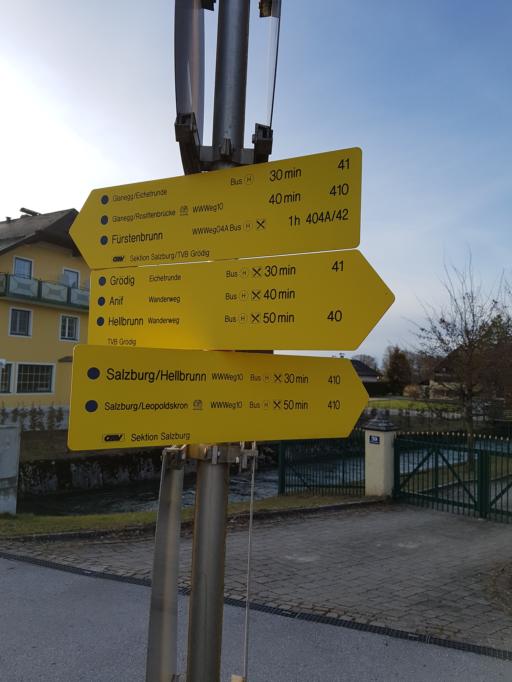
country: AT
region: Salzburg
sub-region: Politischer Bezirk Salzburg-Umgebung
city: Grodig
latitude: 47.7557
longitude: 13.0373
